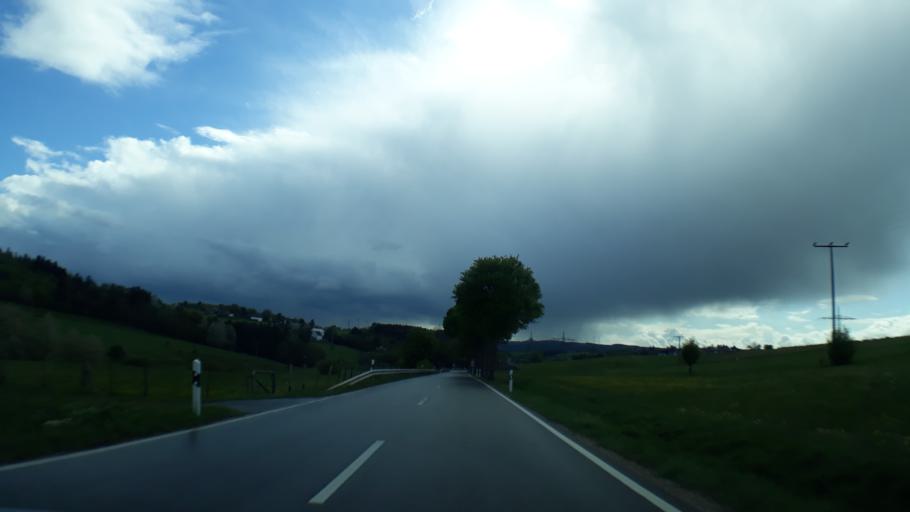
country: DE
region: North Rhine-Westphalia
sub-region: Regierungsbezirk Koln
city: Schleiden
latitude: 50.4915
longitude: 6.4994
